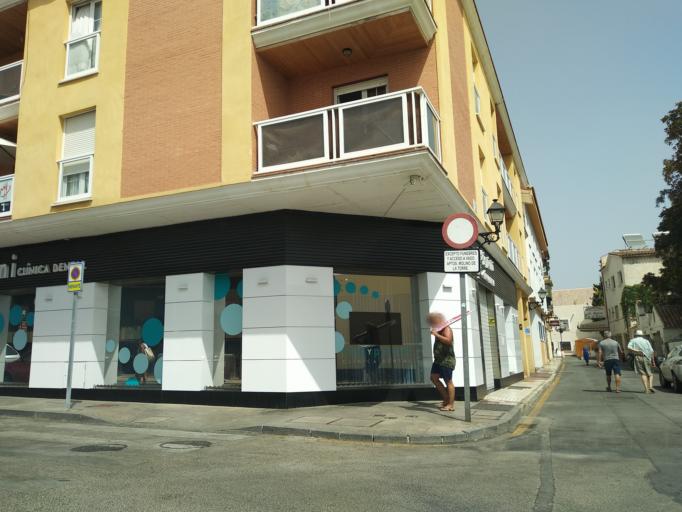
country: ES
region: Andalusia
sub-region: Provincia de Malaga
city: Torremolinos
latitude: 36.6210
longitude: -4.4976
